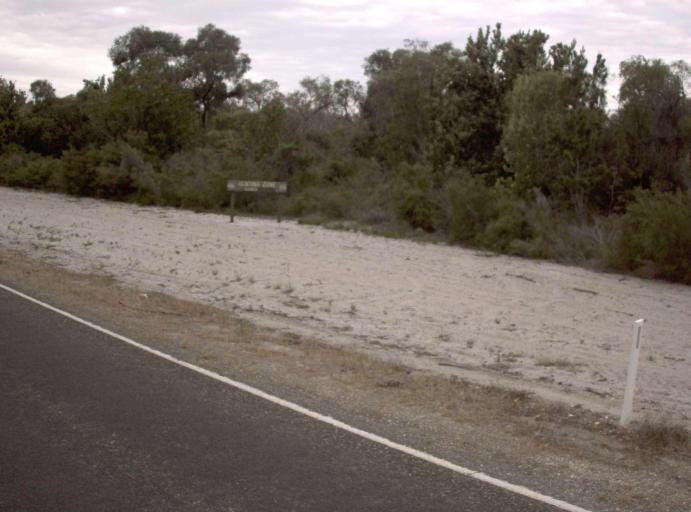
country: AU
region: Victoria
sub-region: Wellington
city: Sale
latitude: -38.1801
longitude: 147.3779
